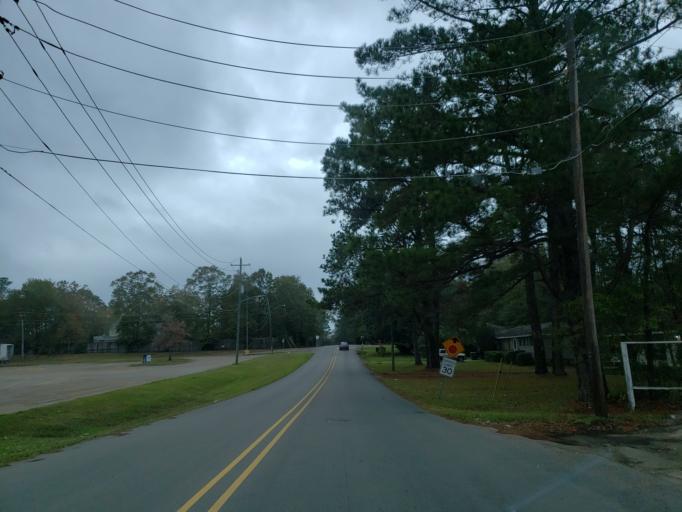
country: US
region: Mississippi
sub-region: Forrest County
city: Hattiesburg
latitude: 31.3127
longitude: -89.3153
